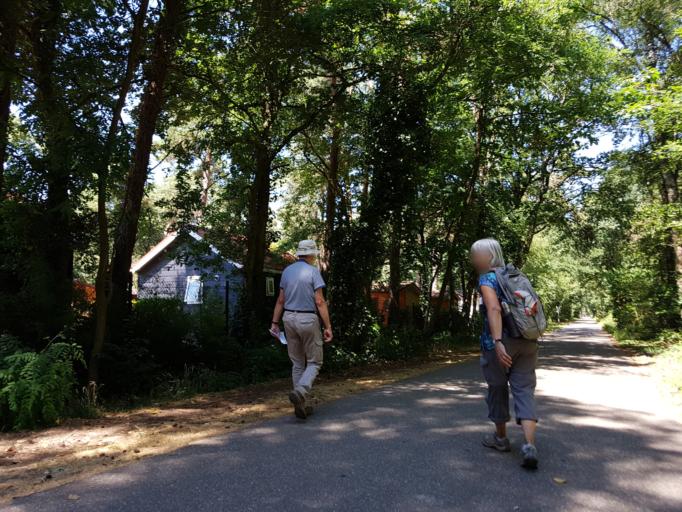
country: NL
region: North Brabant
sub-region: Gemeente Haaren
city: Haaren
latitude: 51.5744
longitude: 5.2351
